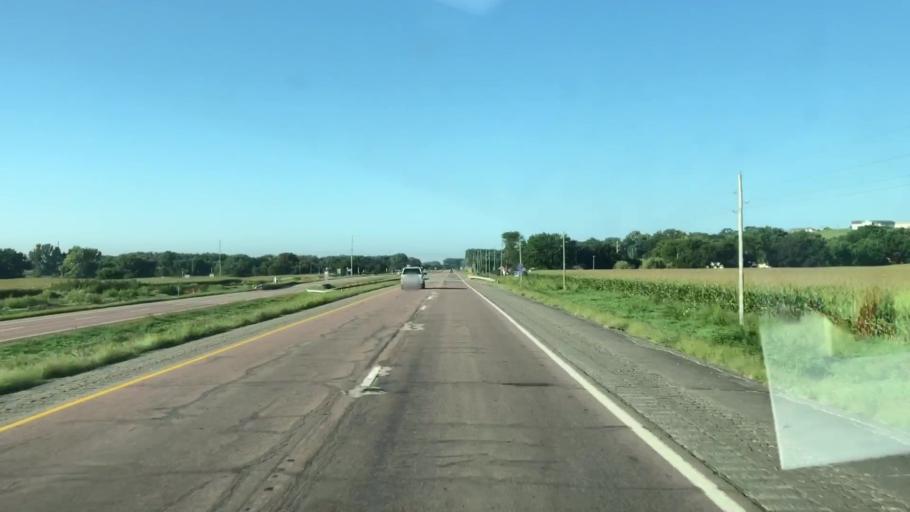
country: US
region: Iowa
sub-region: Woodbury County
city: Sioux City
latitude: 42.5802
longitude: -96.3134
